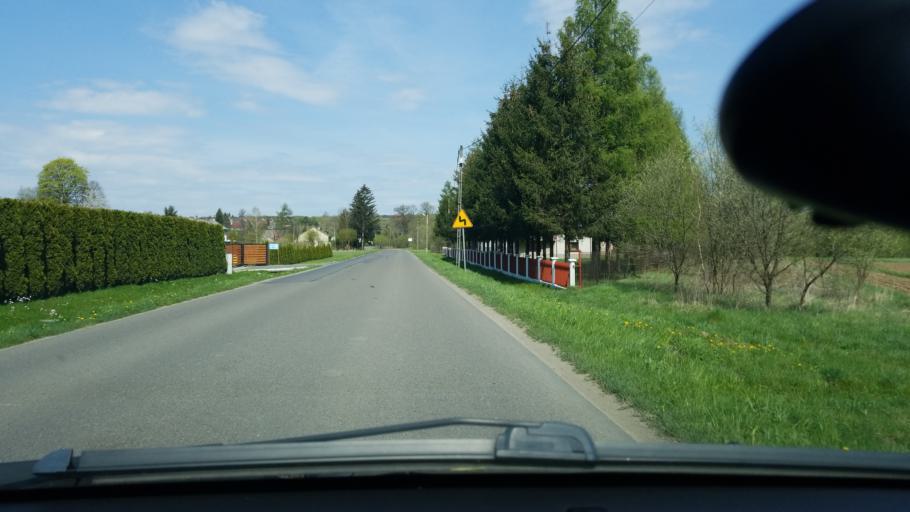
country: PL
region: Subcarpathian Voivodeship
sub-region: Powiat jasielski
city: Debowiec
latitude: 49.7018
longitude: 21.4617
